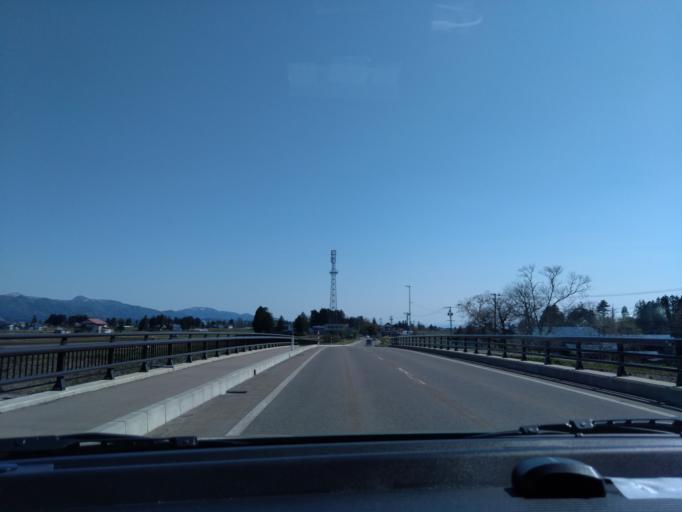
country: JP
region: Akita
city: Kakunodatemachi
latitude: 39.5435
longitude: 140.5856
